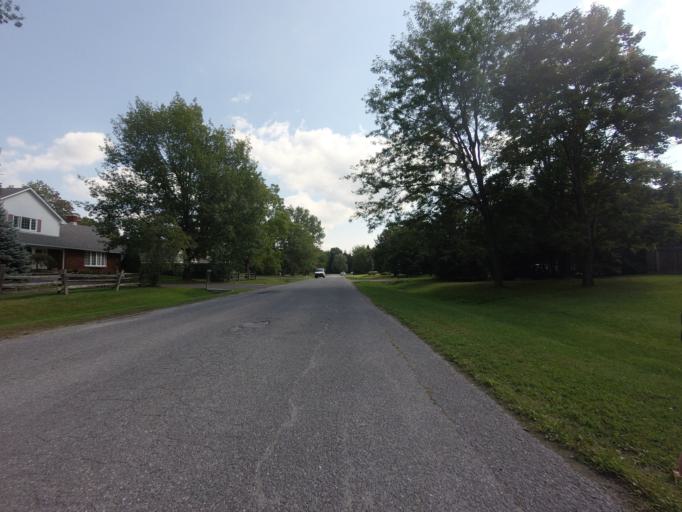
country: CA
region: Ontario
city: Bells Corners
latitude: 45.2346
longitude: -75.6930
